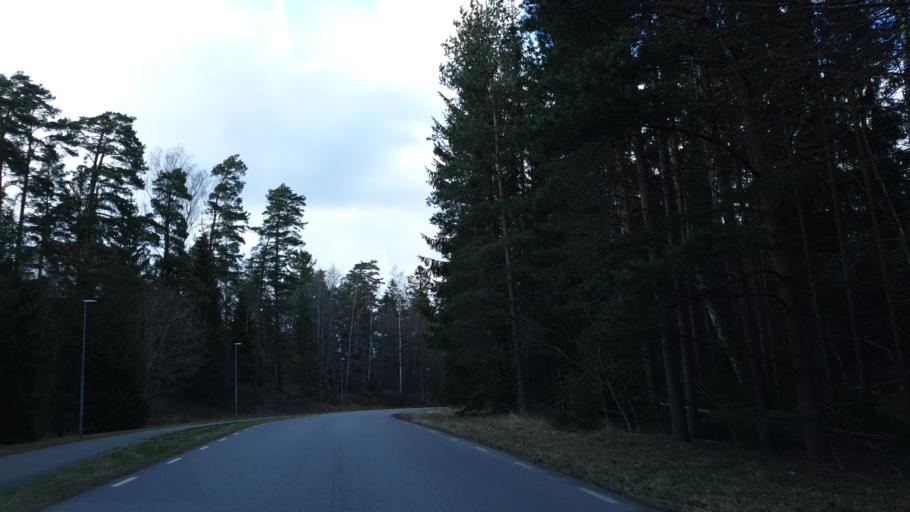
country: SE
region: Stockholm
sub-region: Lidingo
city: Lidingoe
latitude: 59.3861
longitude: 18.1190
